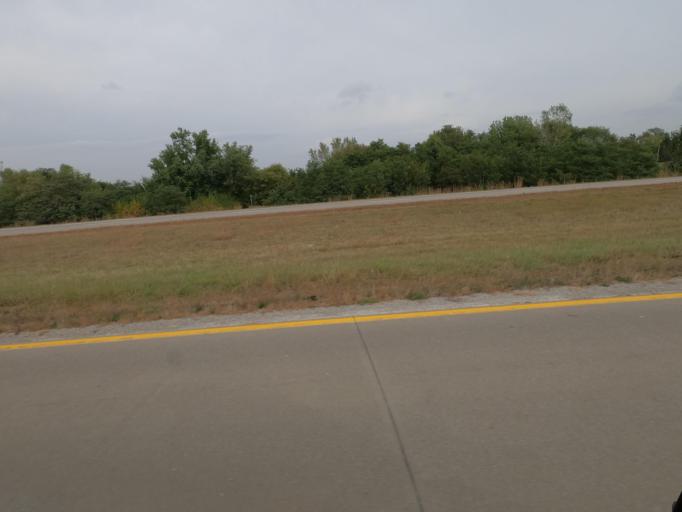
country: US
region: Iowa
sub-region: Mahaska County
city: Oskaloosa
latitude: 41.3466
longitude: -92.7502
